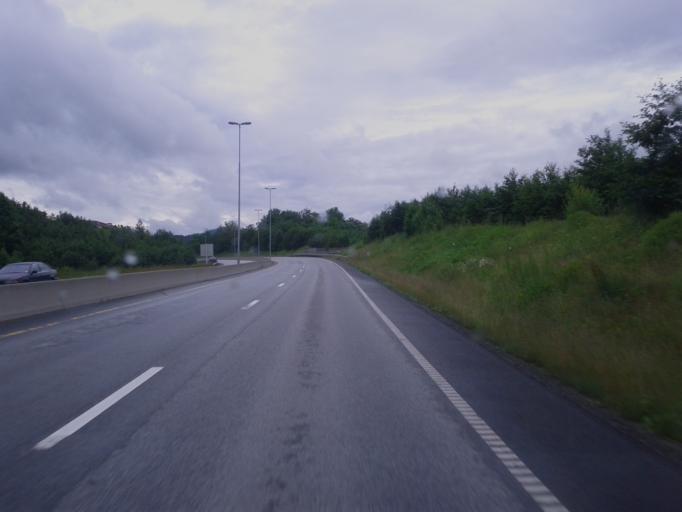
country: NO
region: Sor-Trondelag
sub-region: Melhus
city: Melhus
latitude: 63.2936
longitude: 10.2756
